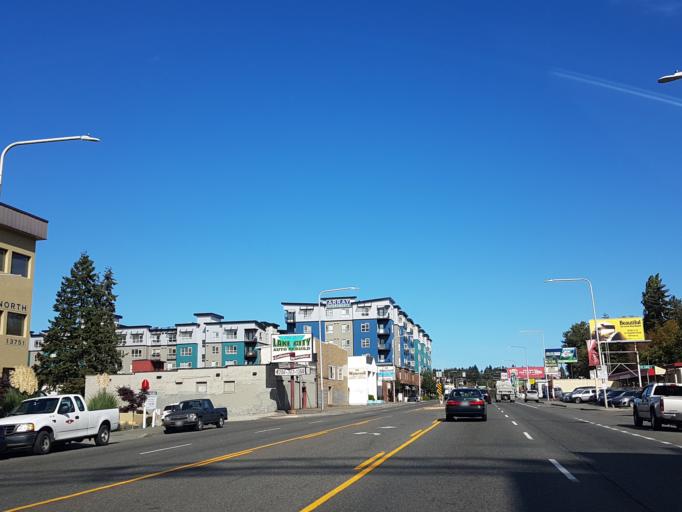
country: US
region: Washington
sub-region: King County
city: Lake Forest Park
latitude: 47.7297
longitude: -122.2923
